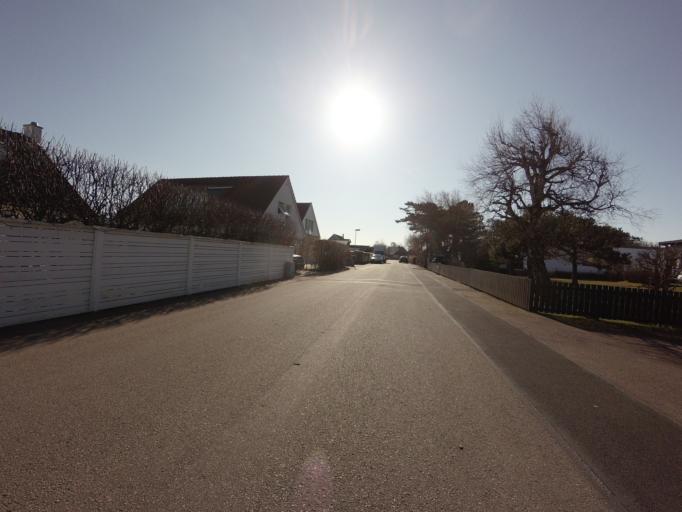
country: SE
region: Skane
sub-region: Hoganas Kommun
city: Hoganas
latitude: 56.1511
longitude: 12.5719
